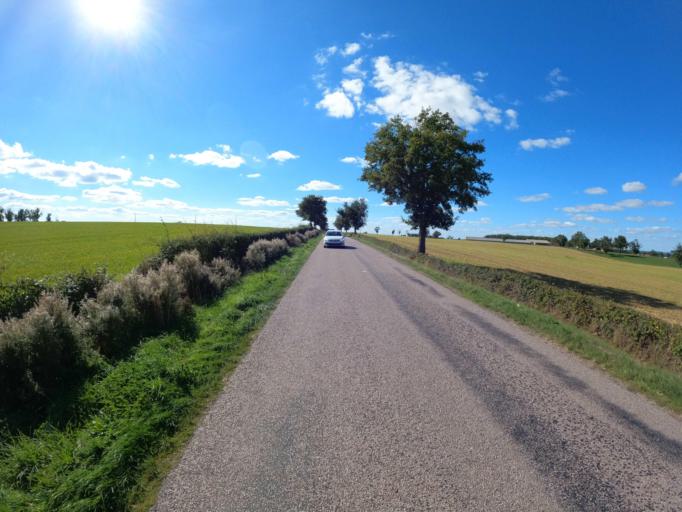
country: FR
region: Auvergne
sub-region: Departement de l'Allier
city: Buxieres-les-Mines
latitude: 46.4032
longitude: 2.9809
